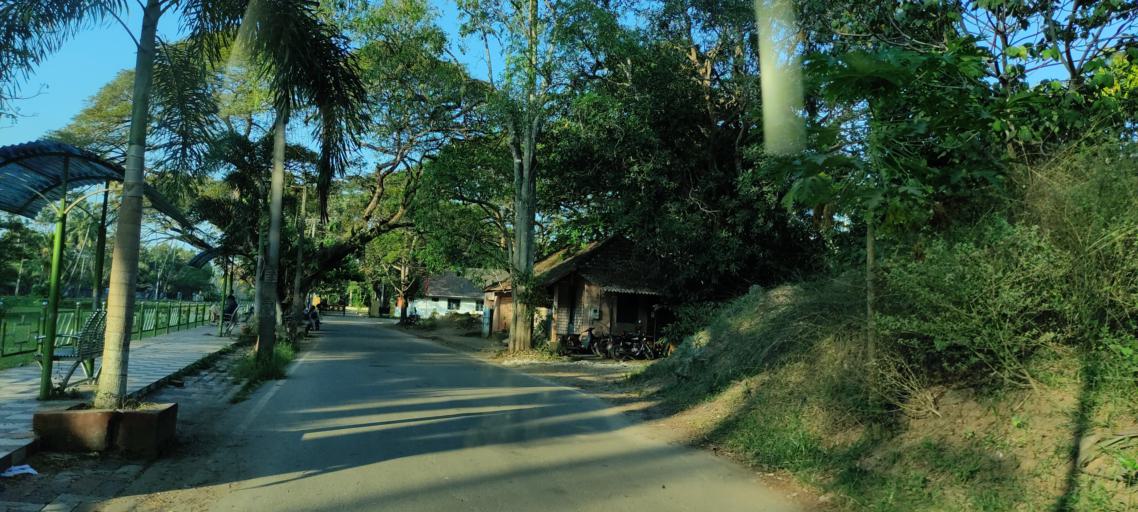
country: IN
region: Kerala
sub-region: Alappuzha
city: Vayalar
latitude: 9.6932
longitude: 76.3436
